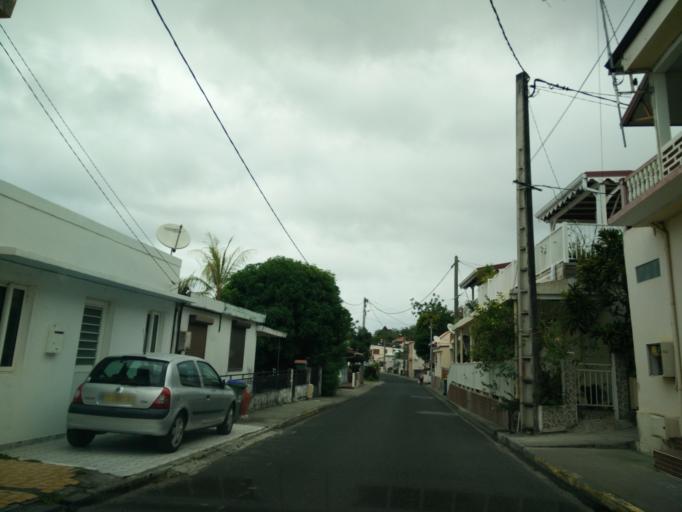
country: MQ
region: Martinique
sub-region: Martinique
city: Saint-Pierre
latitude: 14.7973
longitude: -61.2216
